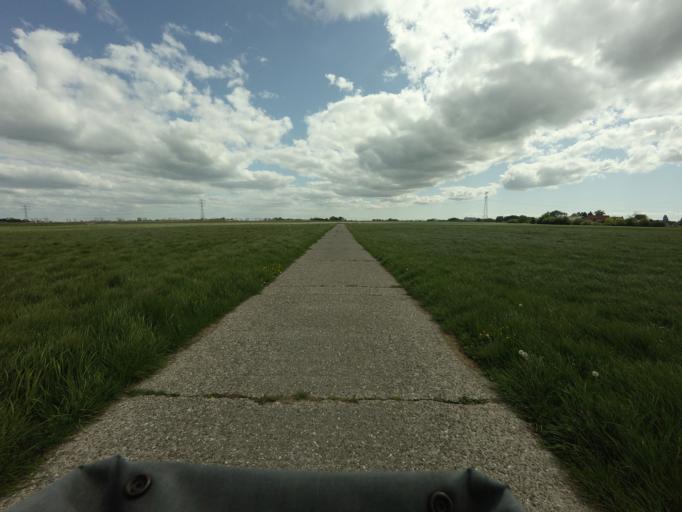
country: NL
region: Friesland
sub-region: Sudwest Fryslan
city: Bolsward
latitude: 53.0759
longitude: 5.5489
